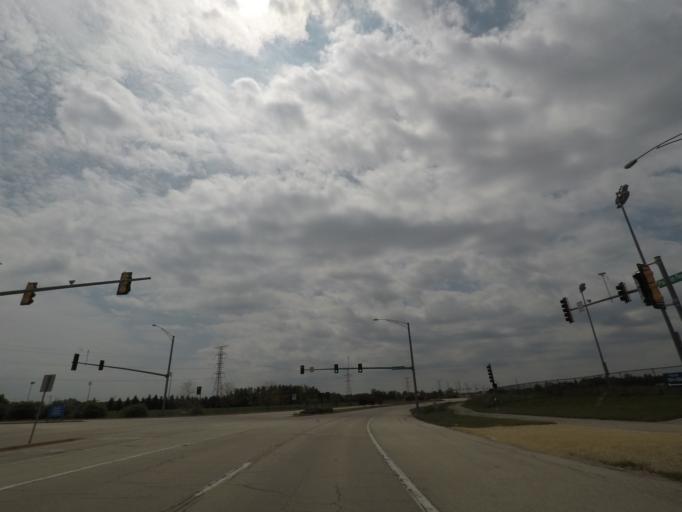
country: US
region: Illinois
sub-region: Winnebago County
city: Cherry Valley
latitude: 42.3222
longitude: -88.9484
